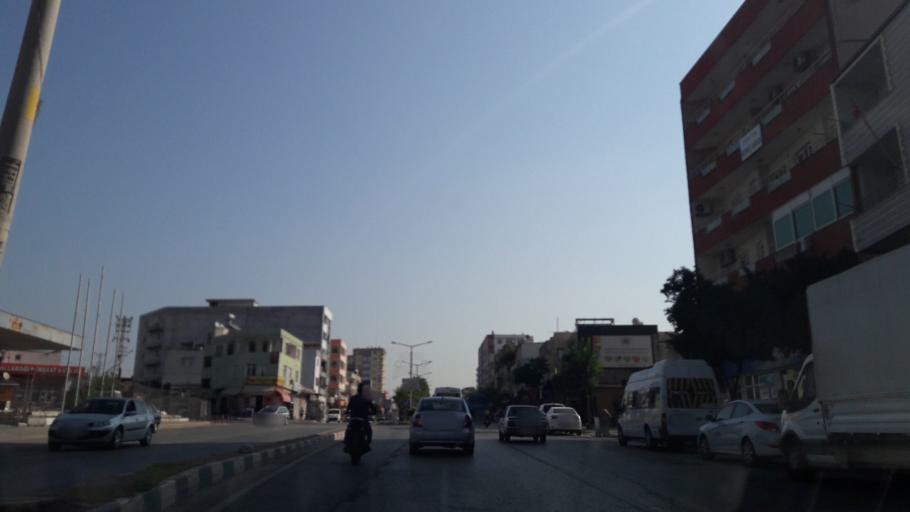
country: TR
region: Adana
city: Yuregir
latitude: 37.0314
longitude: 35.4090
